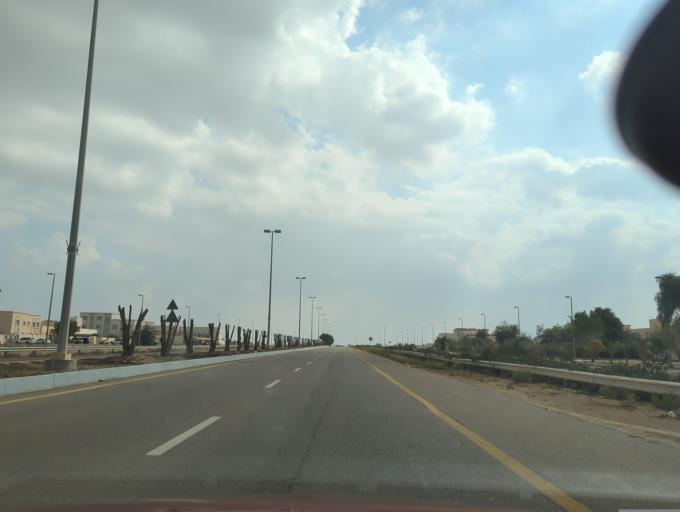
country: AE
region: Abu Dhabi
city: Abu Dhabi
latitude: 24.3707
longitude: 54.7187
